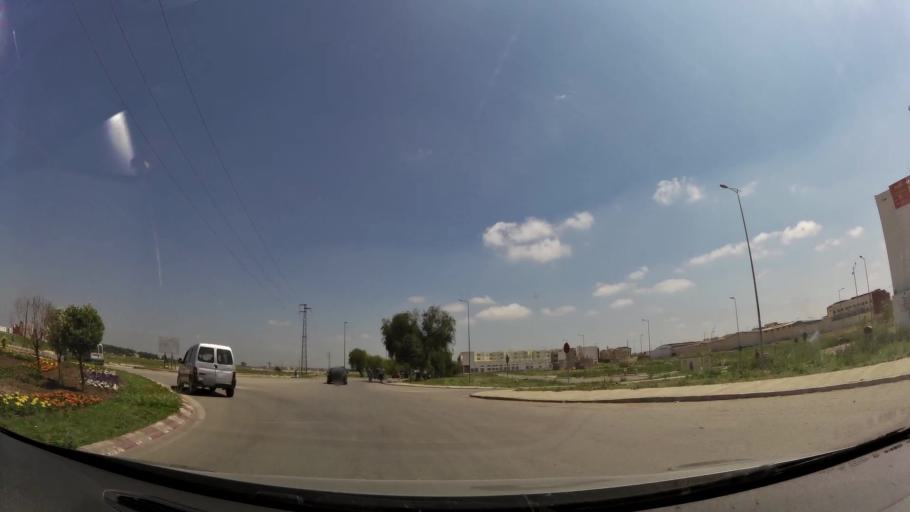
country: MA
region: Fes-Boulemane
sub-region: Fes
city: Fes
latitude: 34.0087
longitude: -5.0463
